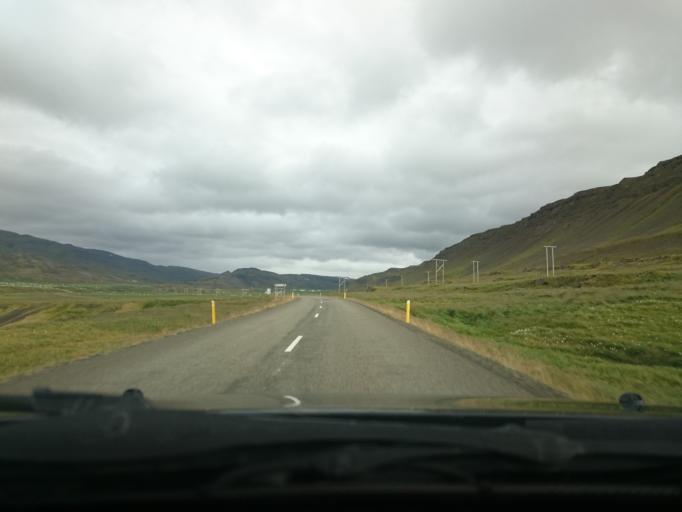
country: IS
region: West
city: Stykkisholmur
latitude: 65.4597
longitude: -21.9154
